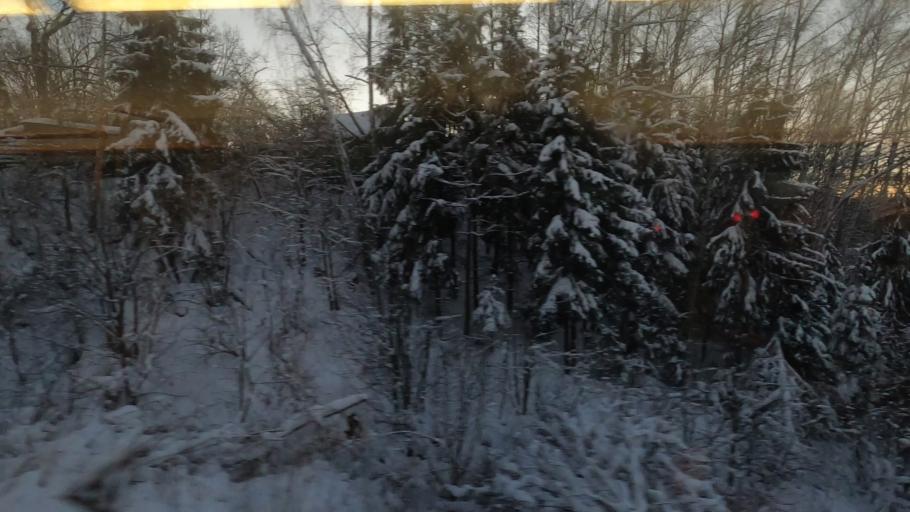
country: RU
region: Moskovskaya
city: Yermolino
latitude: 56.1343
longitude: 37.5181
